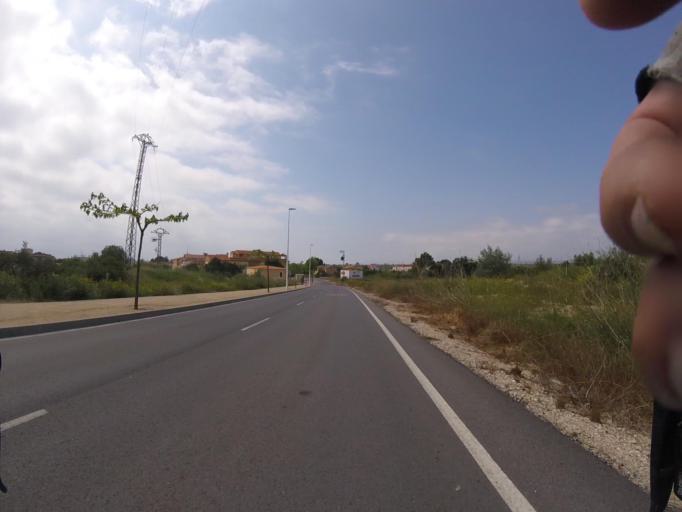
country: ES
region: Valencia
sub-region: Provincia de Castello
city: Alcoceber
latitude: 40.2464
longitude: 0.2714
